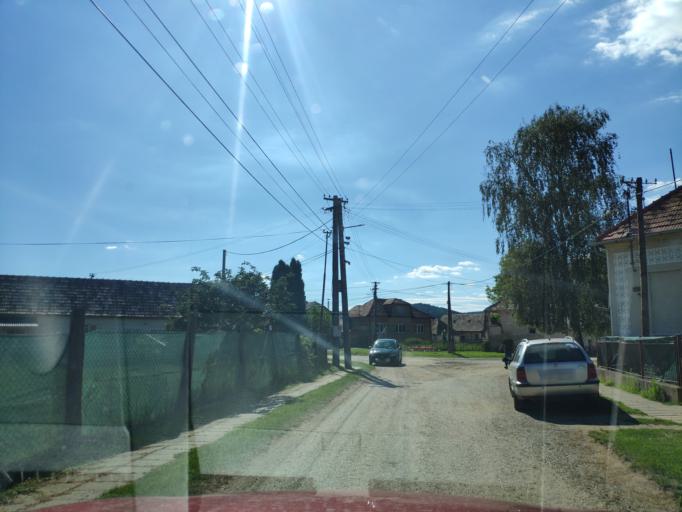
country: SK
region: Banskobystricky
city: Rimavska Sobota
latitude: 48.2631
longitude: 20.1165
